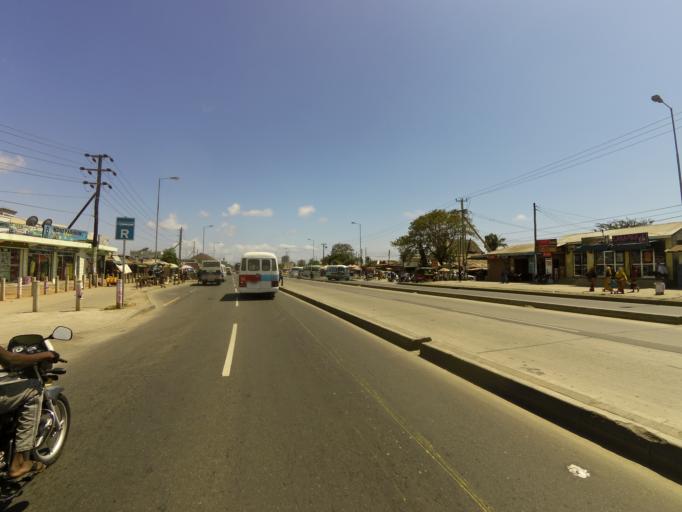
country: TZ
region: Dar es Salaam
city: Magomeni
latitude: -6.7935
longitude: 39.2644
